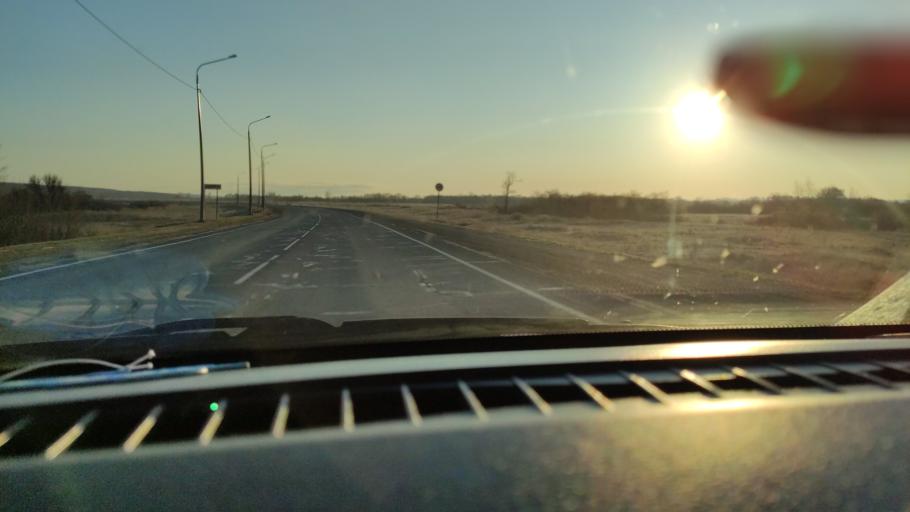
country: RU
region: Saratov
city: Sennoy
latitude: 52.0889
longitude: 46.8084
